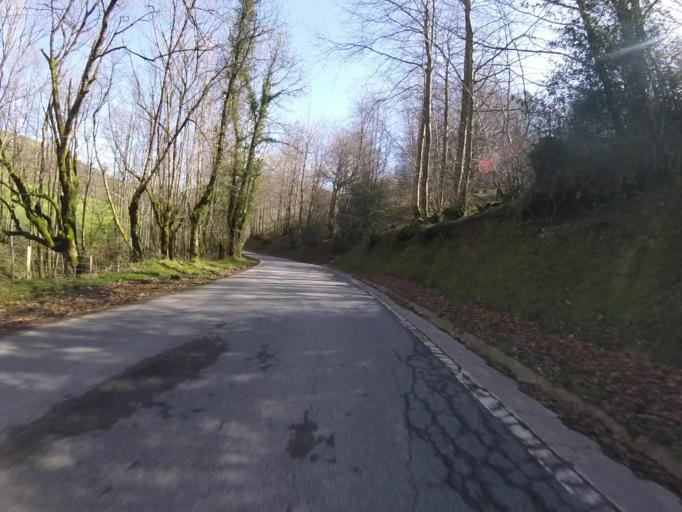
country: ES
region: Navarre
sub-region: Provincia de Navarra
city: Leitza
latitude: 43.0867
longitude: -1.8734
